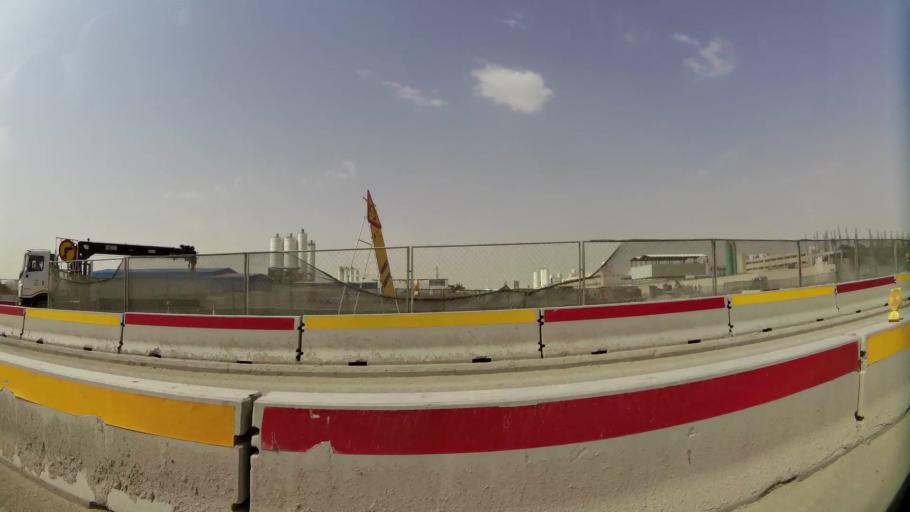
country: QA
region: Al Wakrah
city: Al Wukayr
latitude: 25.1662
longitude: 51.4528
